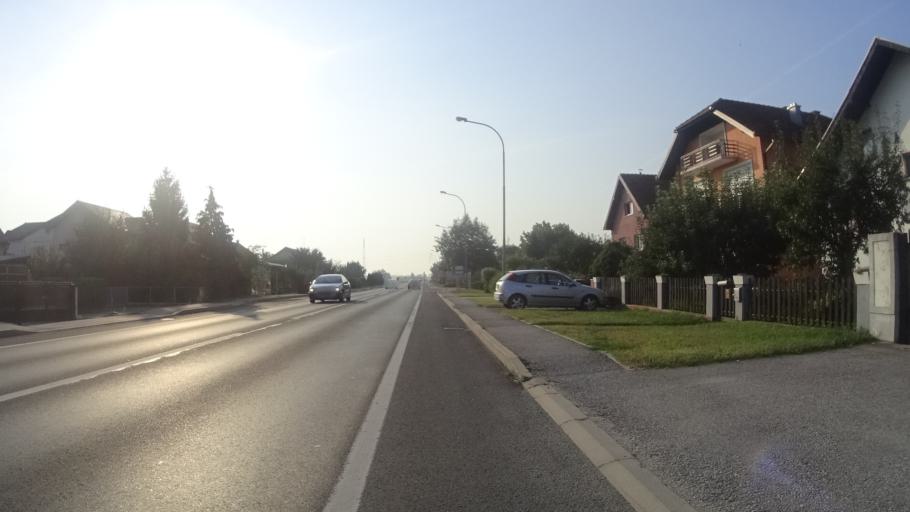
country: HR
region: Varazdinska
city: Sracinec
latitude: 46.3241
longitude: 16.2953
